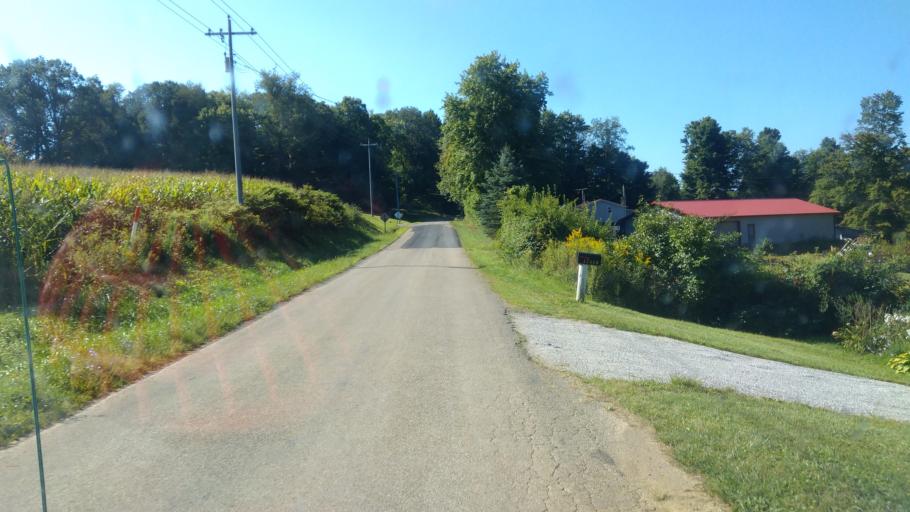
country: US
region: Ohio
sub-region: Knox County
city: Fredericktown
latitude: 40.4828
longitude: -82.4587
